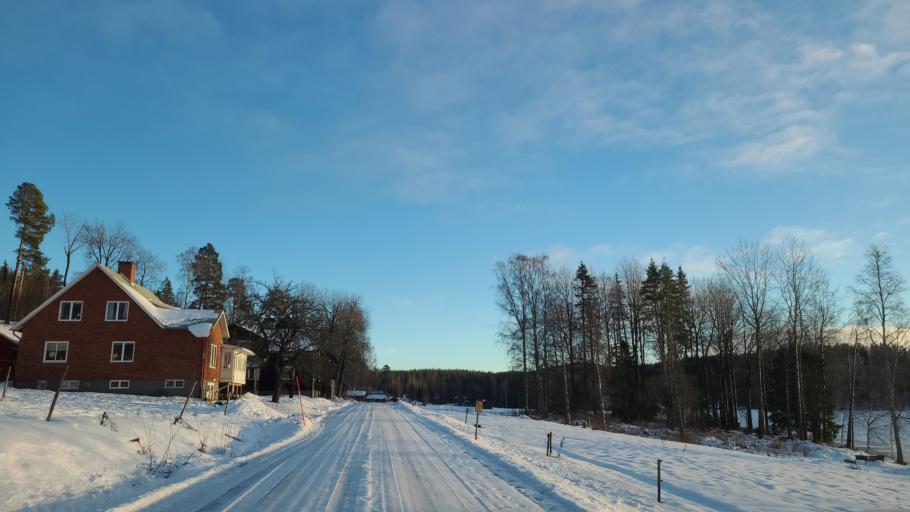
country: SE
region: Gaevleborg
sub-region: Bollnas Kommun
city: Kilafors
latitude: 61.3959
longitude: 16.6801
